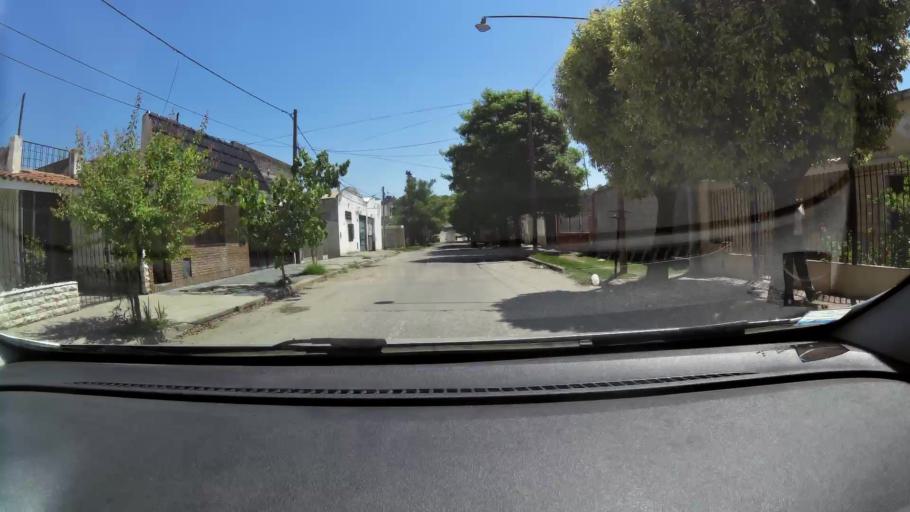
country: AR
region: Cordoba
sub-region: Departamento de Capital
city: Cordoba
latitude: -31.4315
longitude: -64.2034
